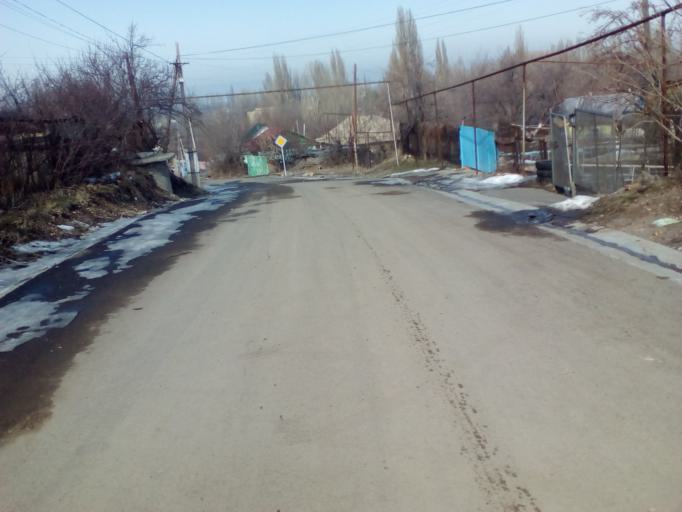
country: KZ
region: Almaty Oblysy
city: Burunday
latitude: 43.1522
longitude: 76.4183
